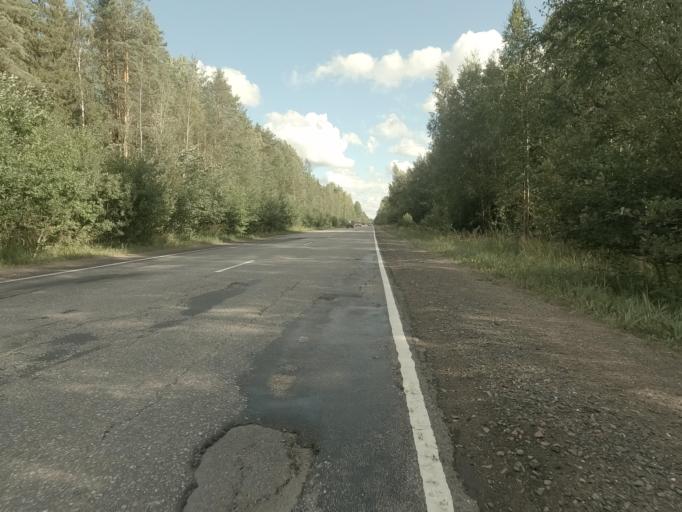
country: RU
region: Leningrad
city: Shcheglovo
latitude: 59.9996
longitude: 30.8720
